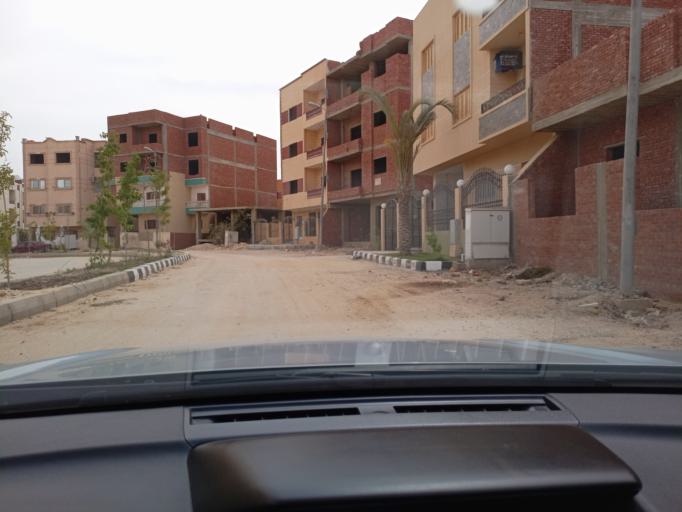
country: EG
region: Muhafazat al Qalyubiyah
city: Al Khankah
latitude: 30.2476
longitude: 31.4974
